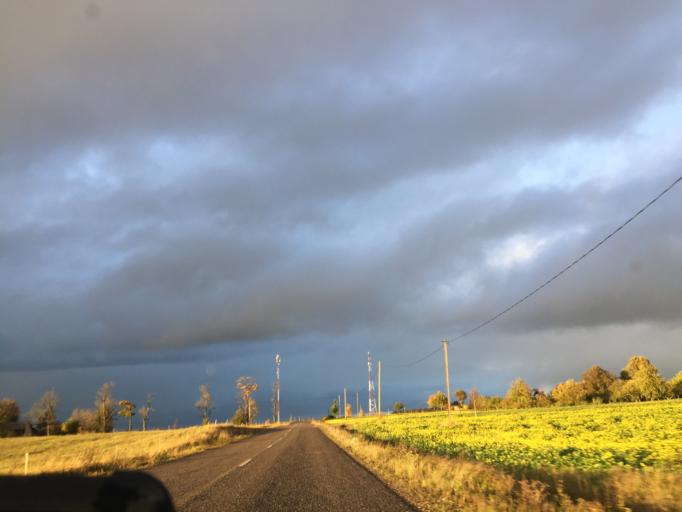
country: LV
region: Talsu Rajons
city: Sabile
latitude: 56.9392
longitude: 22.3966
